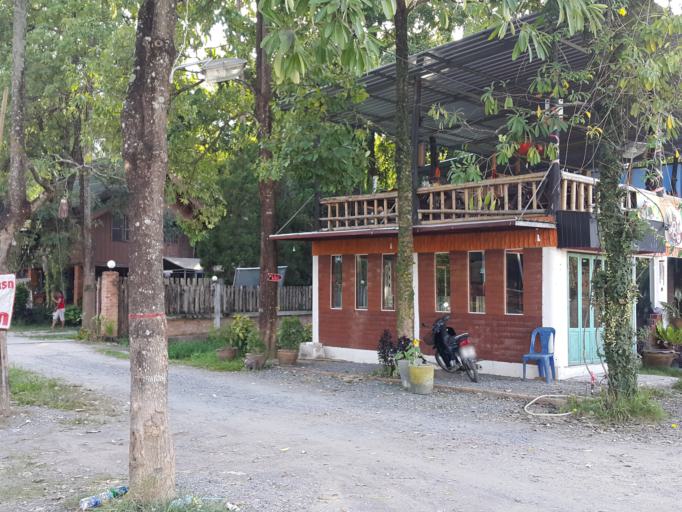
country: TH
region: Chiang Mai
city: Saraphi
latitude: 18.7563
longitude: 99.0509
